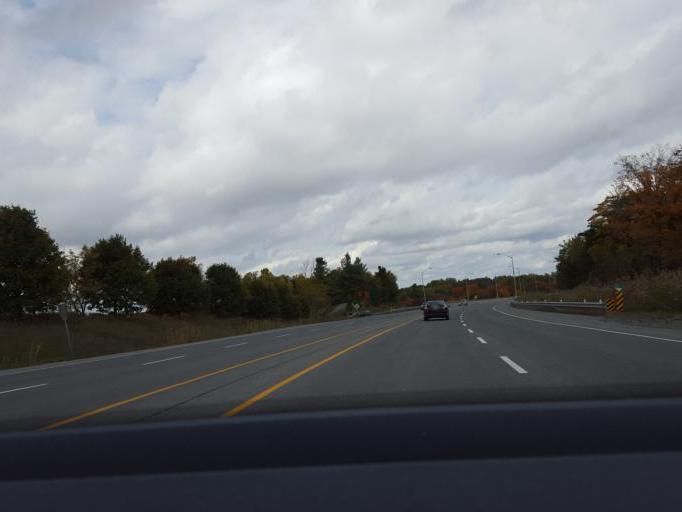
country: CA
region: Ontario
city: Pickering
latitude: 43.8709
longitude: -79.1391
